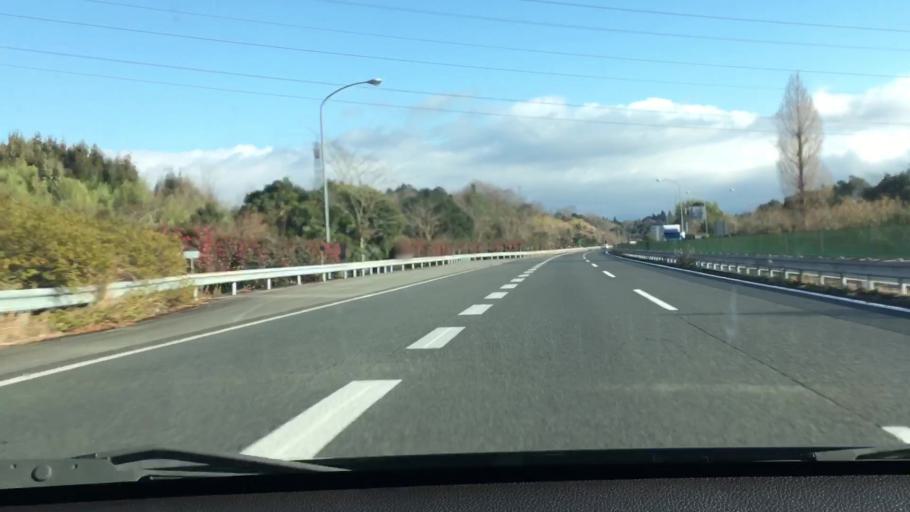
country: JP
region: Kumamoto
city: Hitoyoshi
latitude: 32.2321
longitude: 130.7708
